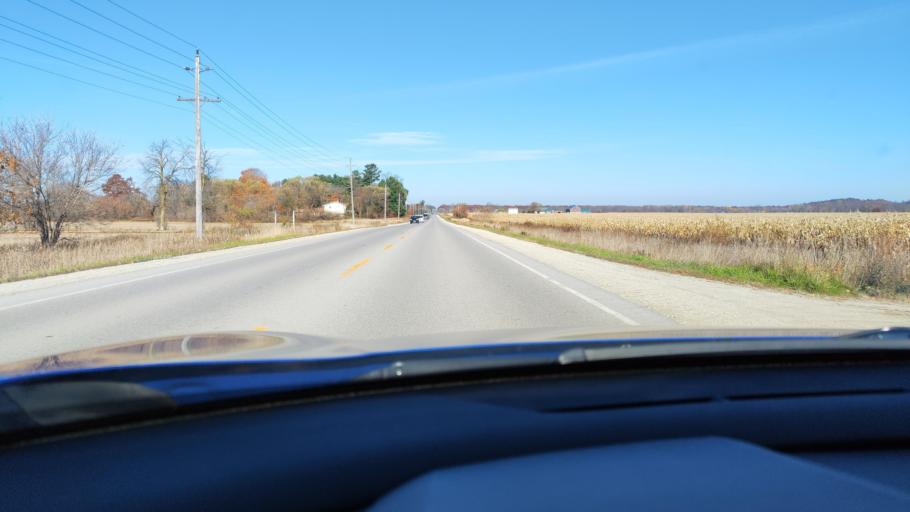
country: CA
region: Ontario
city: Wasaga Beach
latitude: 44.4467
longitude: -80.0689
